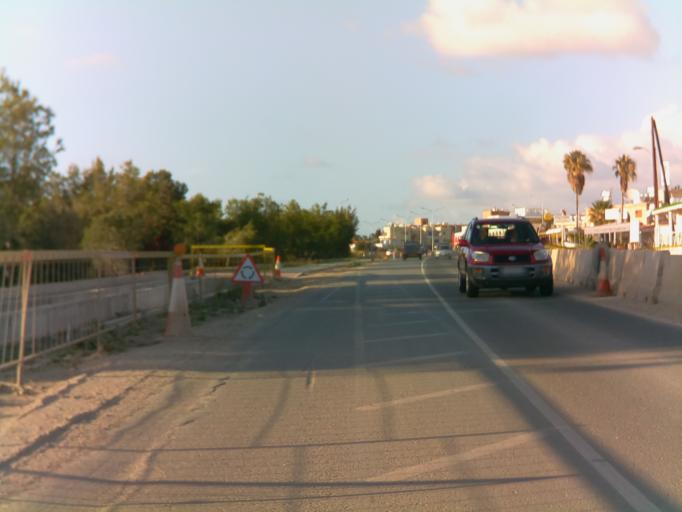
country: CY
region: Pafos
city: Paphos
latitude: 34.7733
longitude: 32.4092
